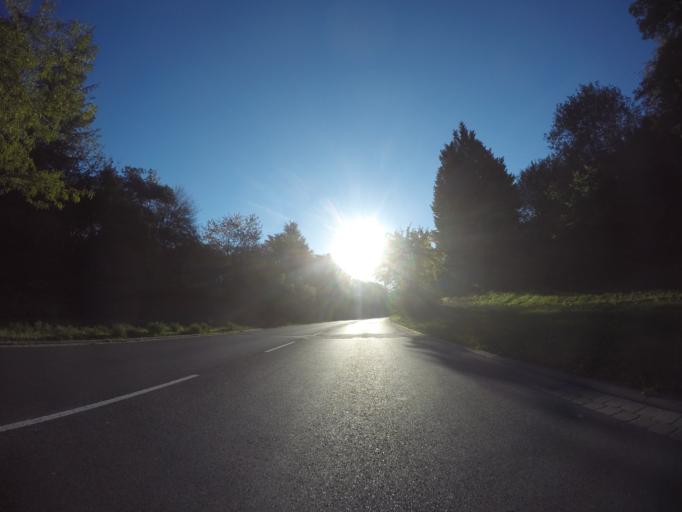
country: DE
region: Bavaria
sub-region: Regierungsbezirk Unterfranken
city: Marktheidenfeld
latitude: 49.8562
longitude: 9.6033
